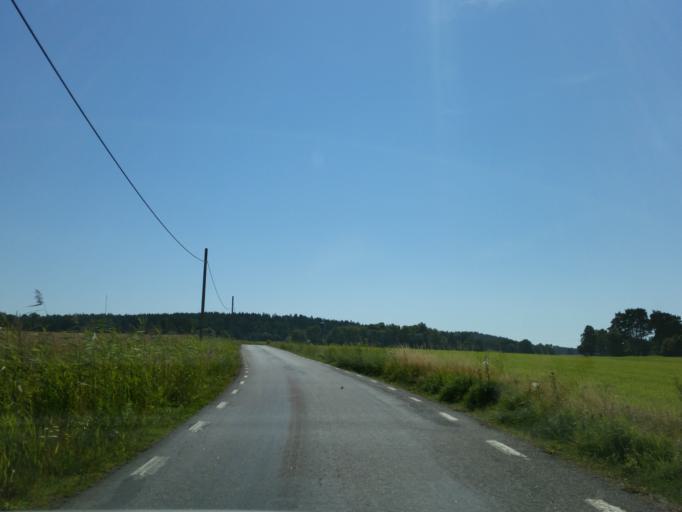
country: SE
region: Soedermanland
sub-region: Trosa Kommun
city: Trosa
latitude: 58.9872
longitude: 17.6549
